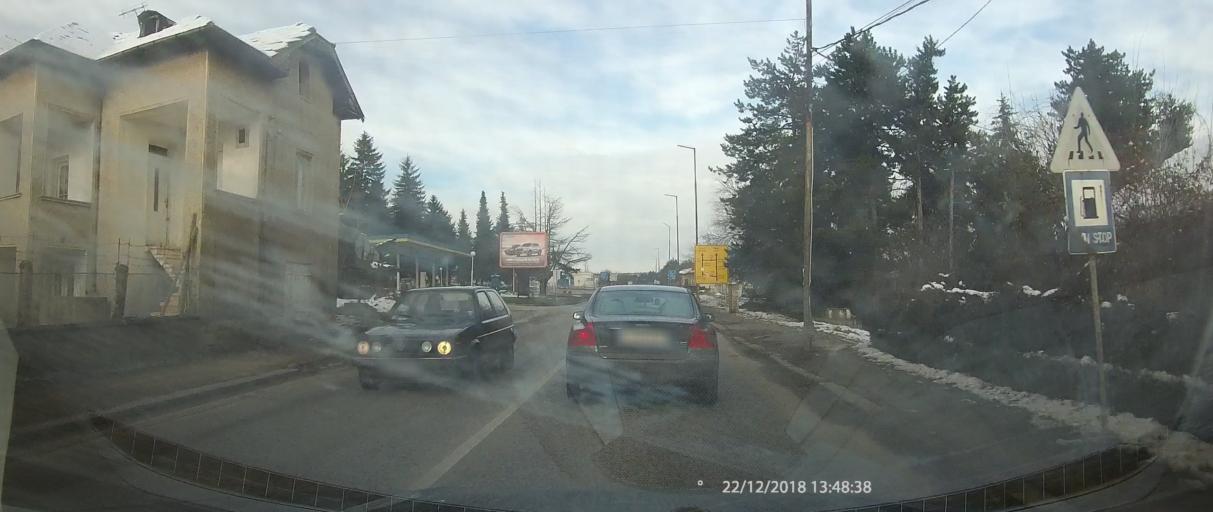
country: BG
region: Lovech
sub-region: Obshtina Lukovit
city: Lukovit
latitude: 43.2522
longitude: 24.1863
